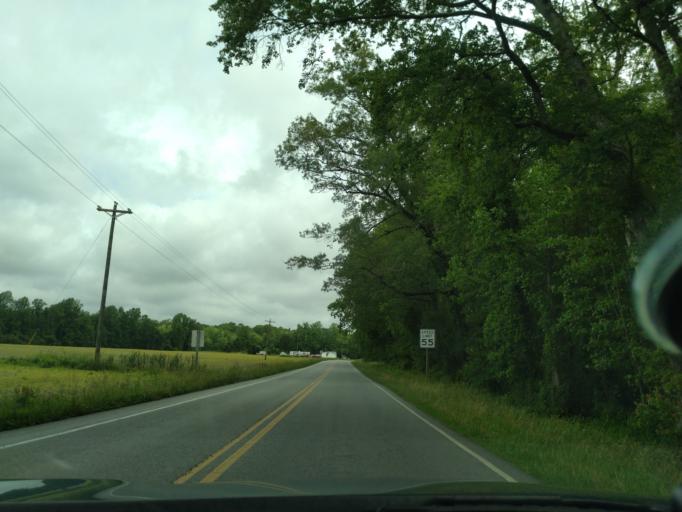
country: US
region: North Carolina
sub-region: Washington County
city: Plymouth
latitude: 35.8449
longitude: -76.7314
